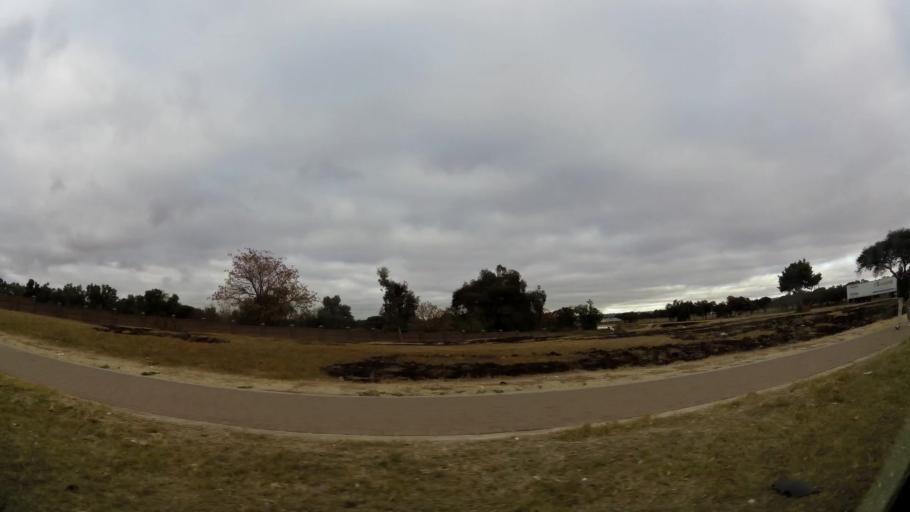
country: ZA
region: Limpopo
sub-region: Capricorn District Municipality
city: Polokwane
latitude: -23.8929
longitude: 29.4369
